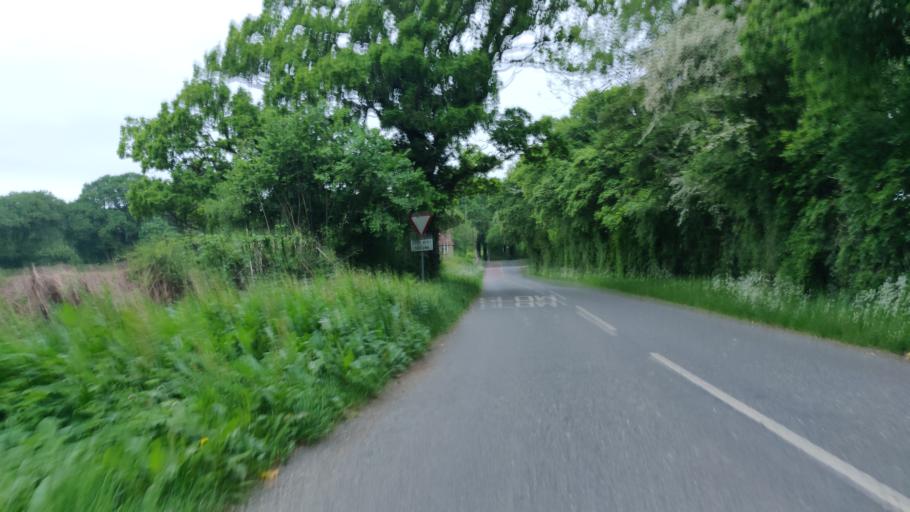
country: GB
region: England
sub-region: West Sussex
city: Partridge Green
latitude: 50.9905
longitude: -0.3038
